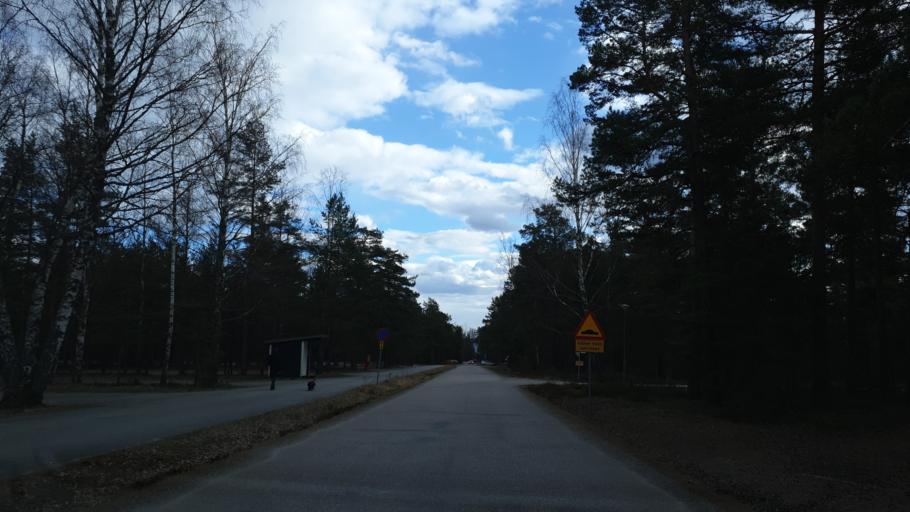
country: SE
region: Stockholm
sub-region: Varmdo Kommun
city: Hemmesta
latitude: 59.2203
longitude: 18.5229
